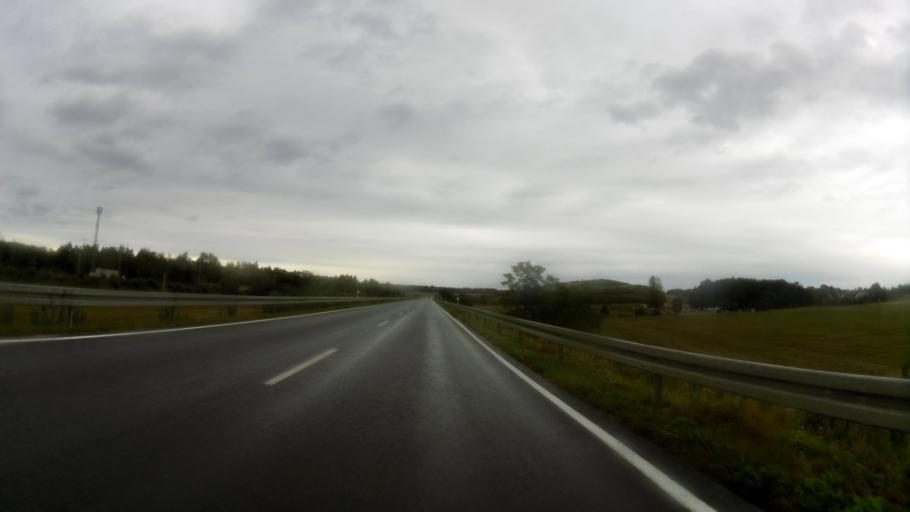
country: DE
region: Brandenburg
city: Spremberg
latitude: 51.5868
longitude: 14.3508
